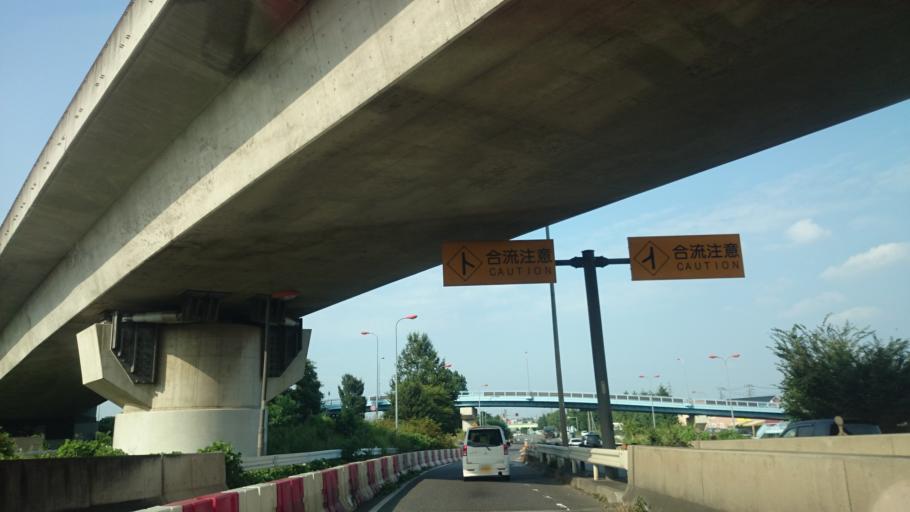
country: JP
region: Saitama
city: Ageoshimo
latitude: 35.9289
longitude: 139.5924
